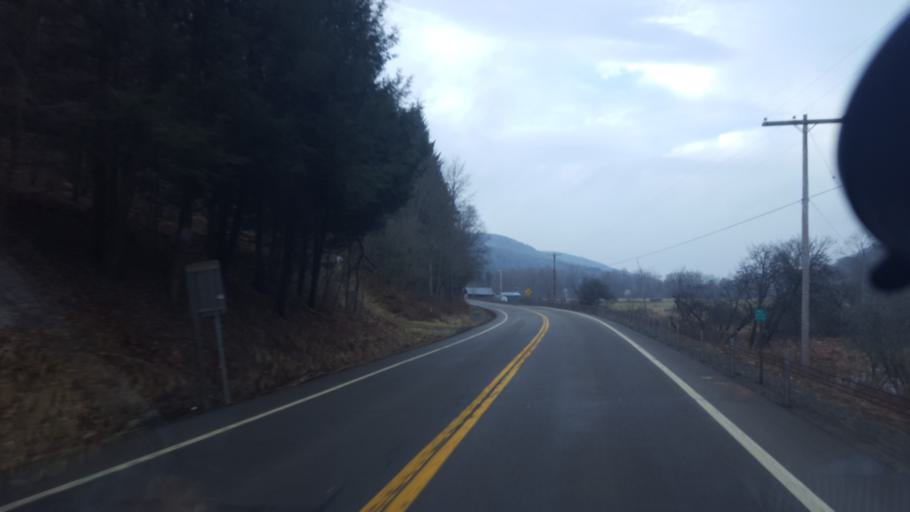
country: US
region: New York
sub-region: Allegany County
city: Andover
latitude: 42.0427
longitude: -77.7596
